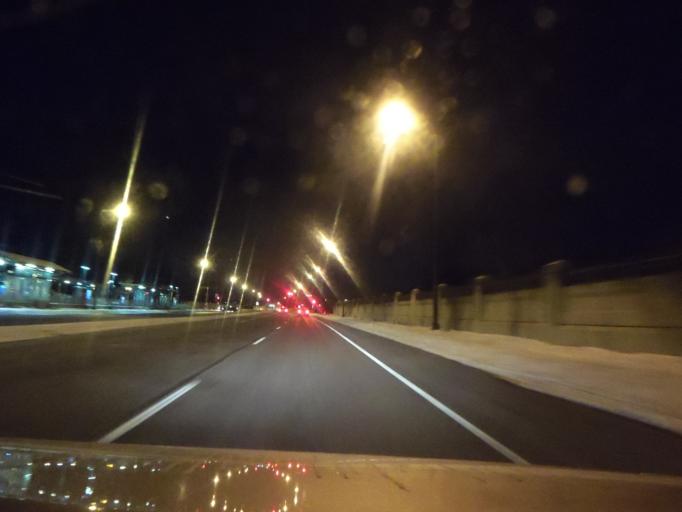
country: US
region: Minnesota
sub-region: Dakota County
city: Mendota Heights
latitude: 44.9119
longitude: -93.2091
